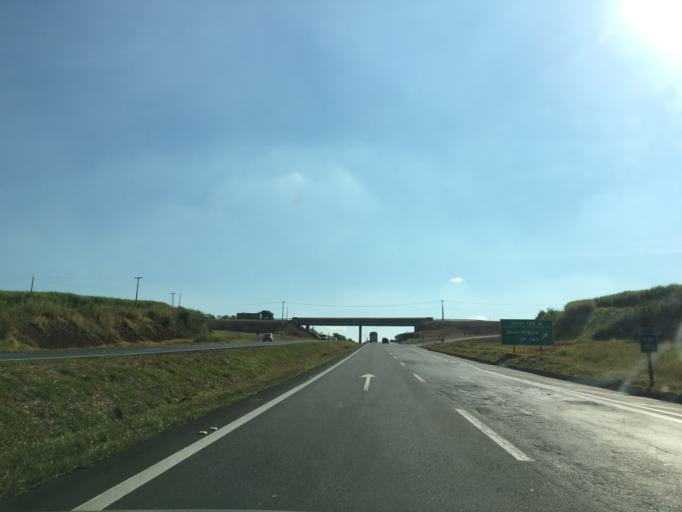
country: BR
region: Sao Paulo
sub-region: Piracicaba
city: Piracicaba
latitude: -22.7242
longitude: -47.5815
